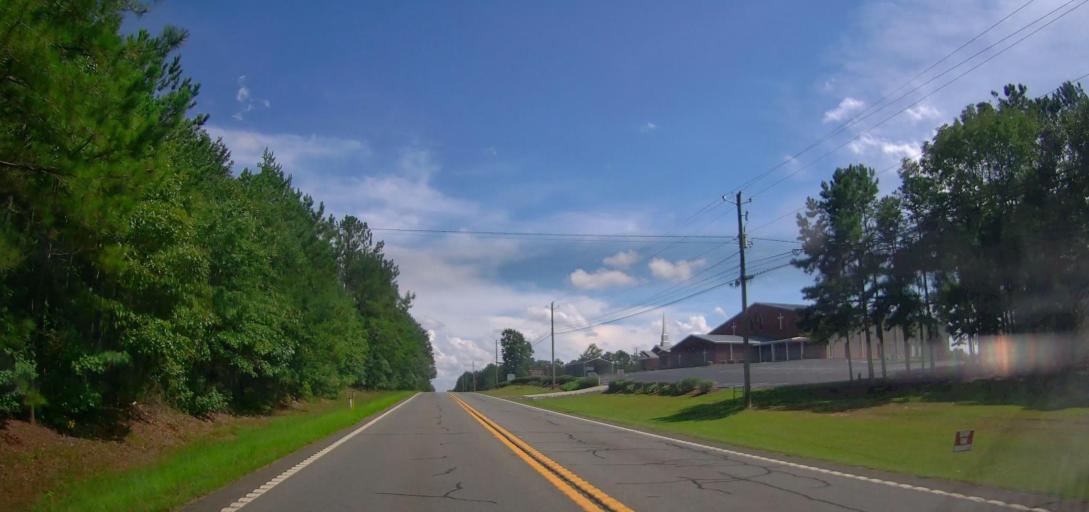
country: US
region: Georgia
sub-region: Talbot County
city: Sardis
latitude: 32.8141
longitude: -84.6003
